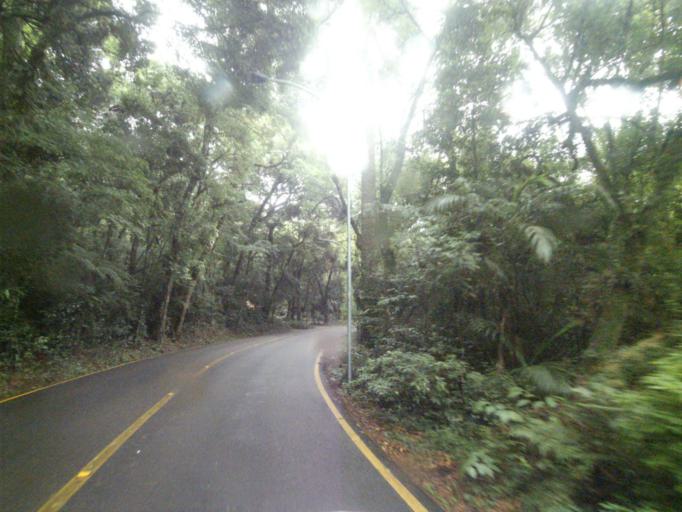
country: BR
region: Parana
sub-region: Curitiba
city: Curitiba
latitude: -25.4240
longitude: -49.3096
